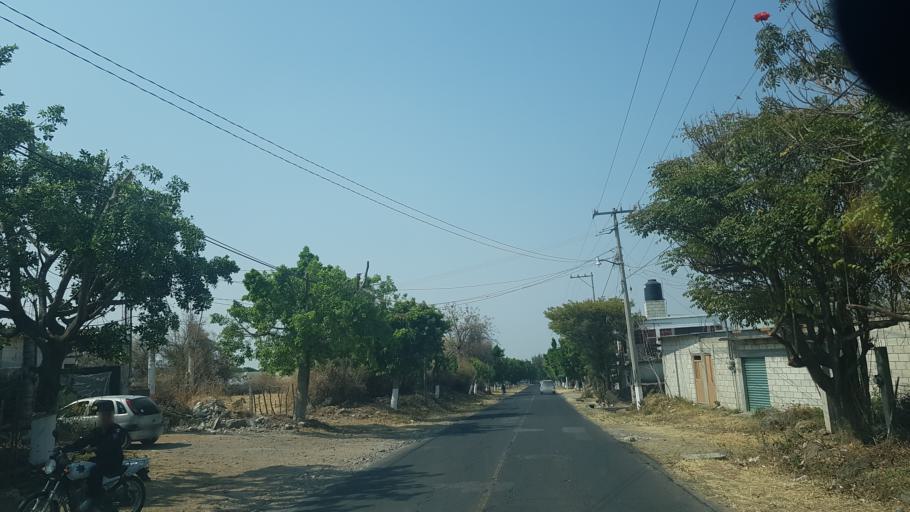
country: MX
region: Morelos
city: Tlacotepec
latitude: 18.8000
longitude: -98.7632
